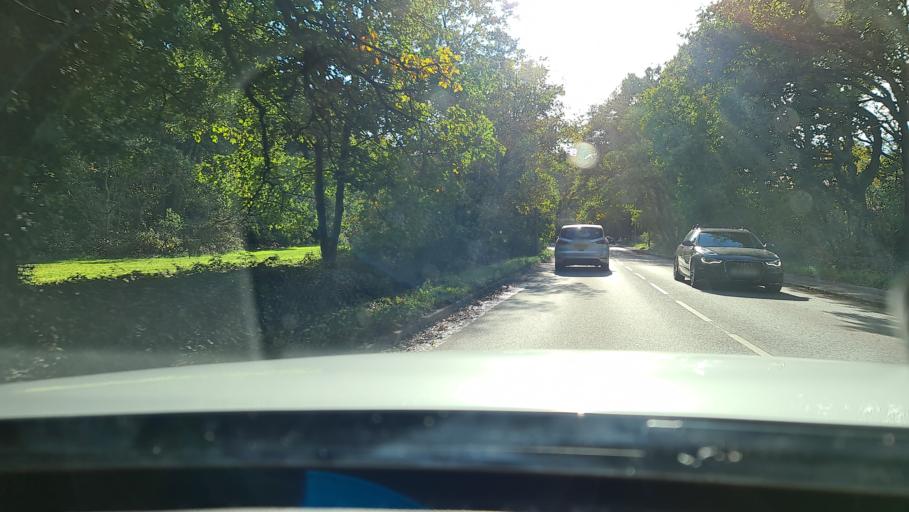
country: GB
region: England
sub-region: Surrey
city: Walton-on-Thames
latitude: 51.3668
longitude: -0.4300
